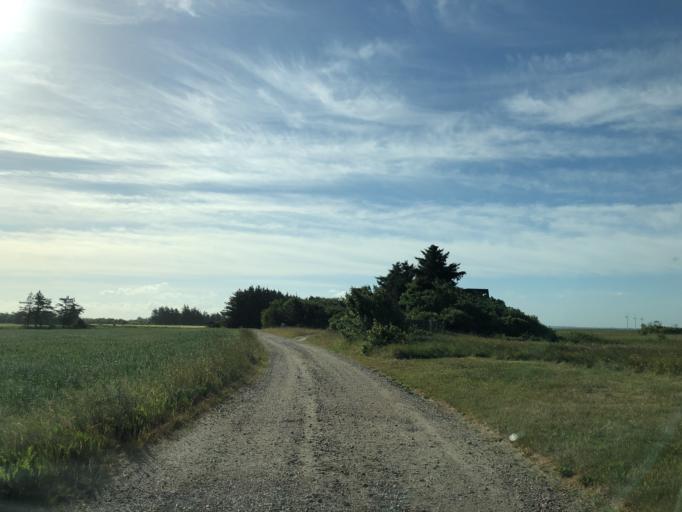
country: DK
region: Central Jutland
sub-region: Holstebro Kommune
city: Ulfborg
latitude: 56.3335
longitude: 8.2688
